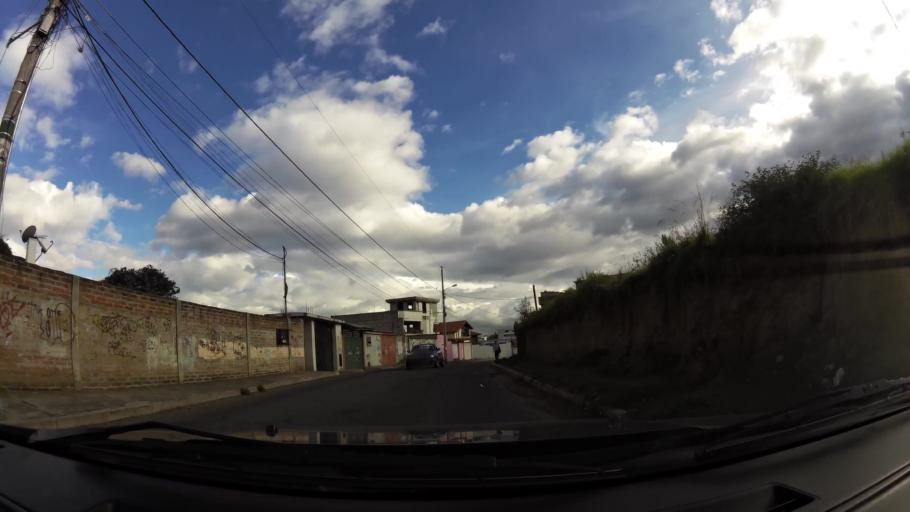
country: EC
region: Pichincha
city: Quito
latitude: -0.1376
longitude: -78.4581
